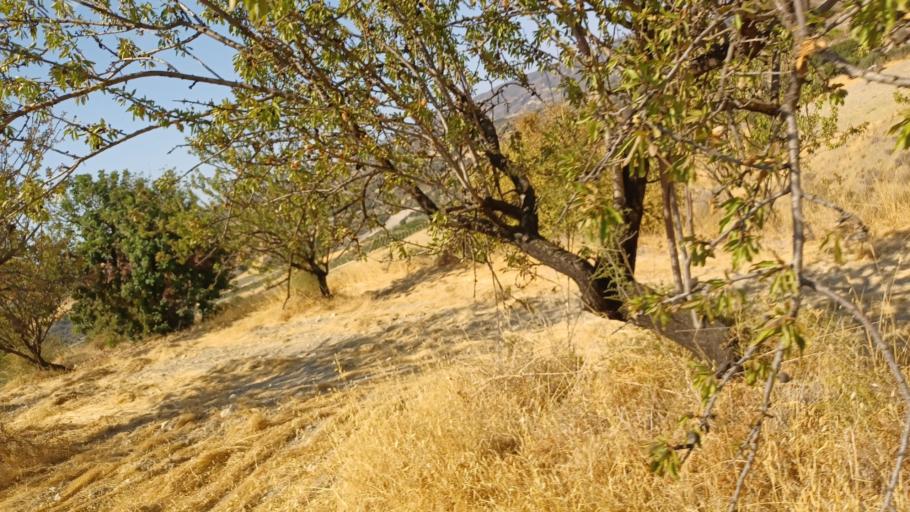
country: CY
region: Pafos
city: Polis
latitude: 34.9656
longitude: 32.4973
